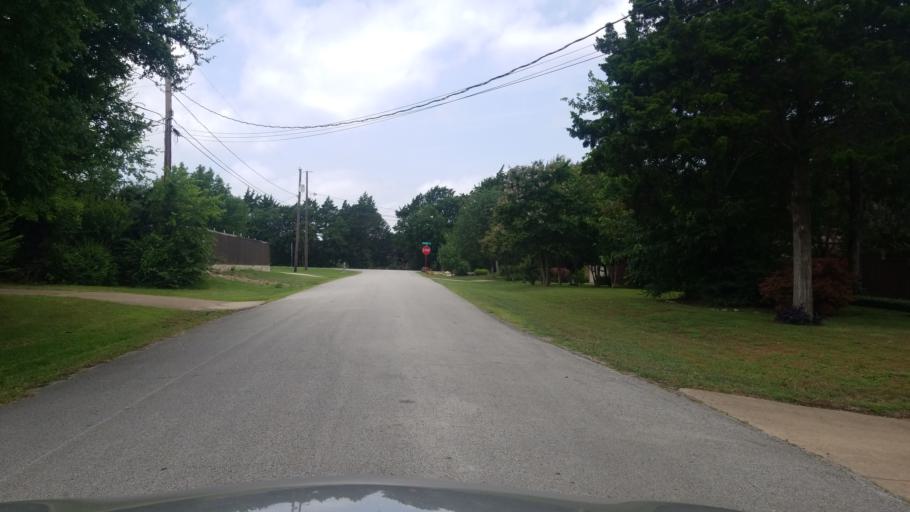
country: US
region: Texas
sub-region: Dallas County
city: Duncanville
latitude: 32.6846
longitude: -96.9331
